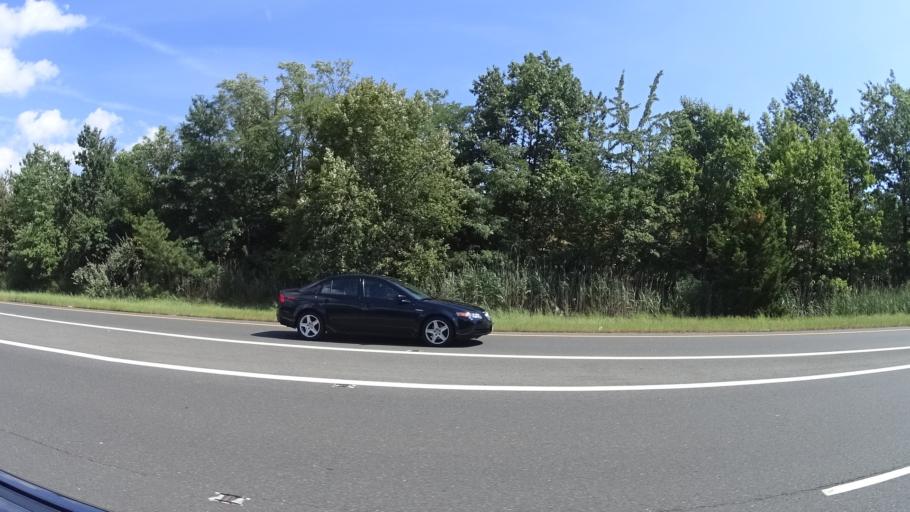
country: US
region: New Jersey
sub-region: Monmouth County
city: Eatontown
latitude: 40.2791
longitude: -74.0748
